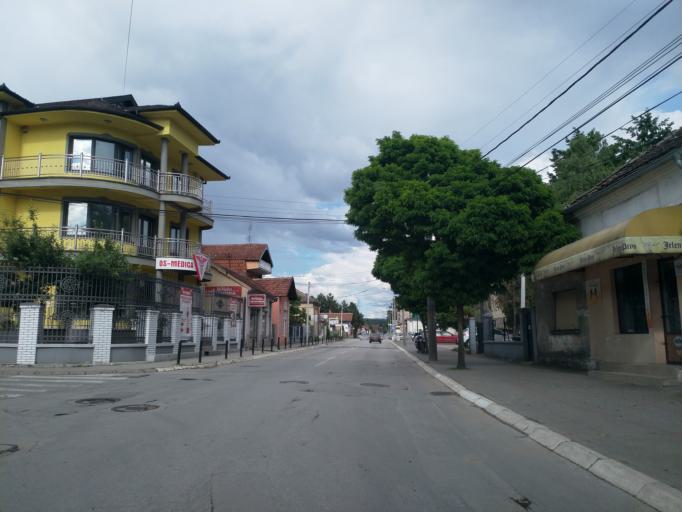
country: RS
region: Central Serbia
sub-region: Pomoravski Okrug
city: Paracin
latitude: 43.8645
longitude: 21.4129
